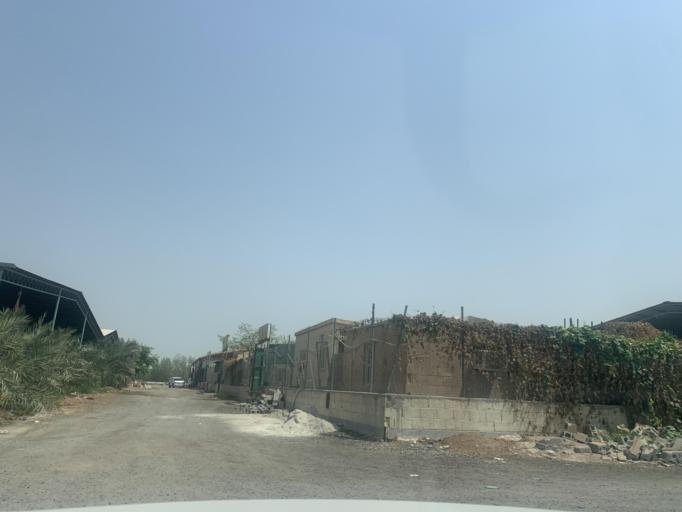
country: BH
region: Central Governorate
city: Madinat Hamad
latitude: 26.1421
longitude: 50.4785
